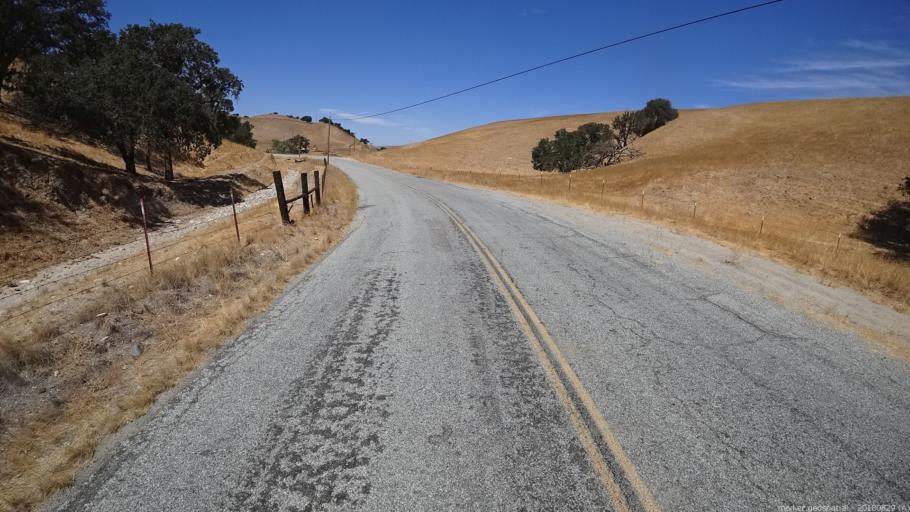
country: US
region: California
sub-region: San Luis Obispo County
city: Lake Nacimiento
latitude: 35.8705
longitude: -120.8361
